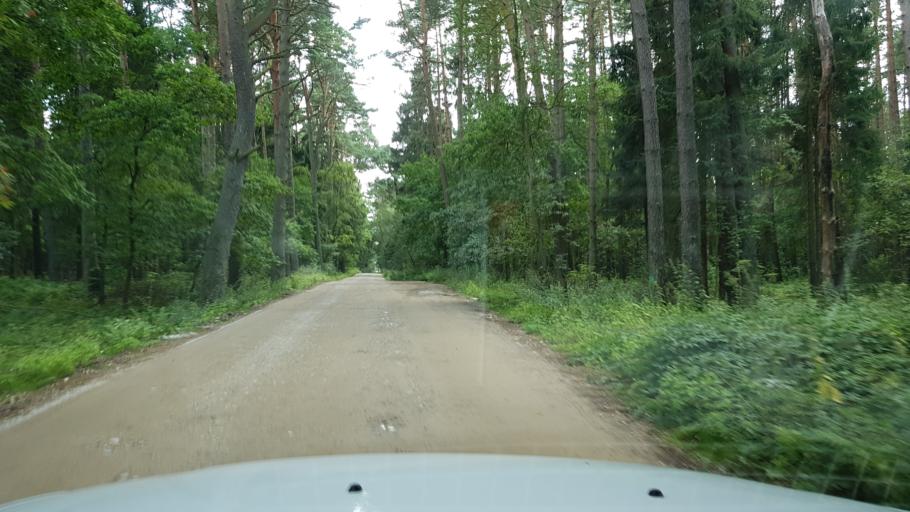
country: PL
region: West Pomeranian Voivodeship
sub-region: Powiat gryficki
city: Pobierowo
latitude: 54.0487
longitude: 14.9056
